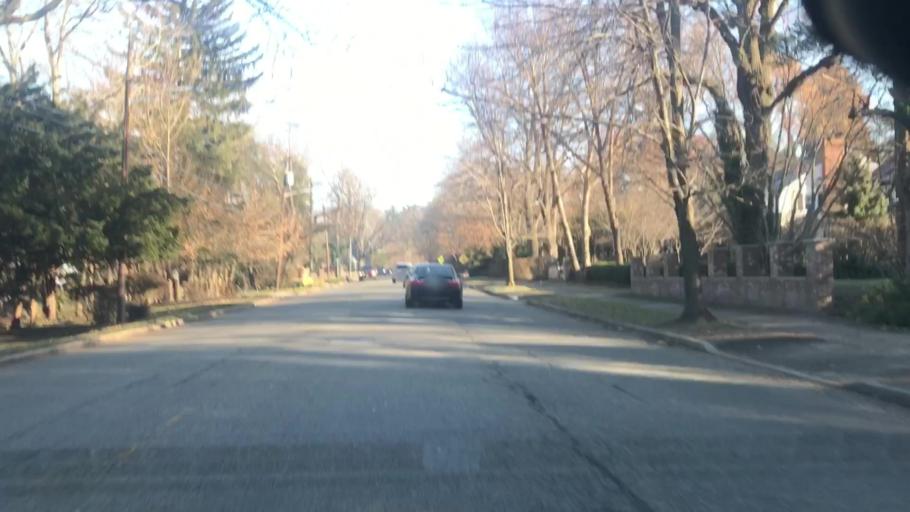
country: US
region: New Jersey
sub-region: Bergen County
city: Englewood
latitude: 40.8815
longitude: -73.9737
